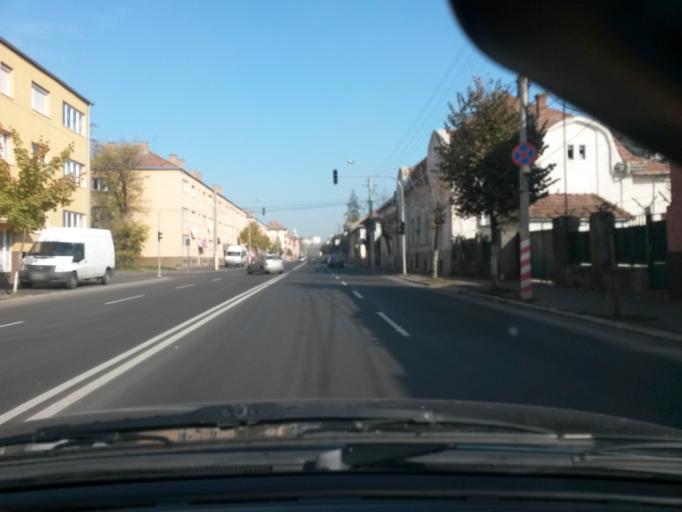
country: RO
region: Mures
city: Targu-Mures
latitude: 46.5341
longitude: 24.5533
